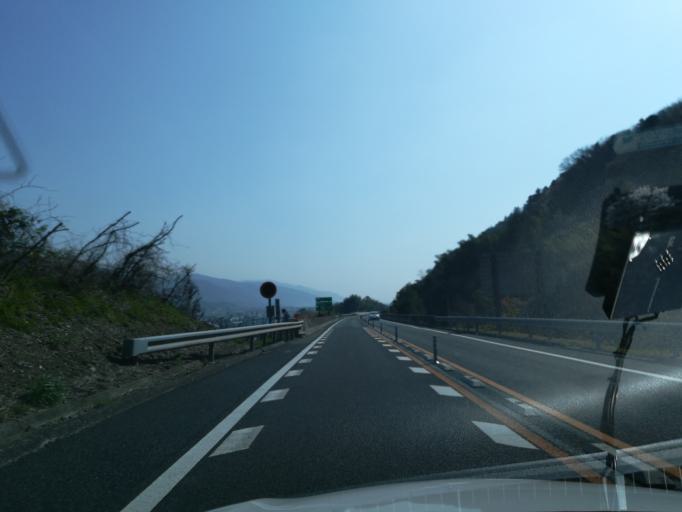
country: JP
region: Tokushima
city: Ikedacho
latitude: 34.0310
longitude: 133.8515
